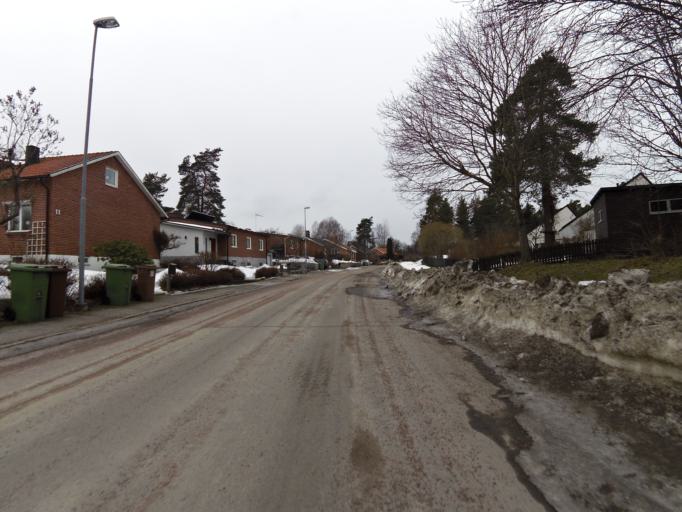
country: SE
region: Gaevleborg
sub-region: Gavle Kommun
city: Gavle
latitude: 60.6592
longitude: 17.1326
